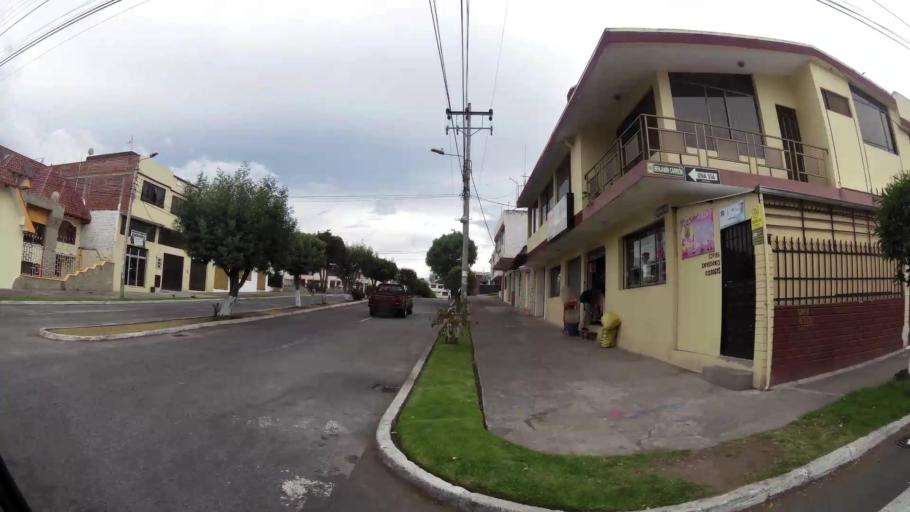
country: EC
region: Tungurahua
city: Ambato
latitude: -1.2599
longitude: -78.6314
